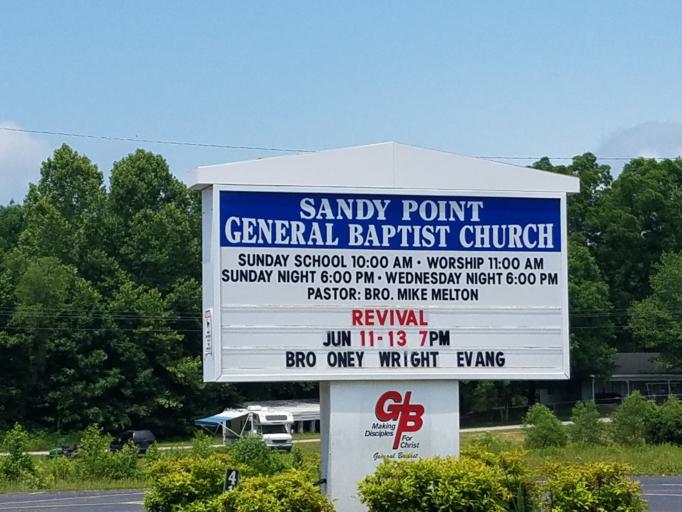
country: US
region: Tennessee
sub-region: Benton County
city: Camden
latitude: 36.0458
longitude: -88.1632
